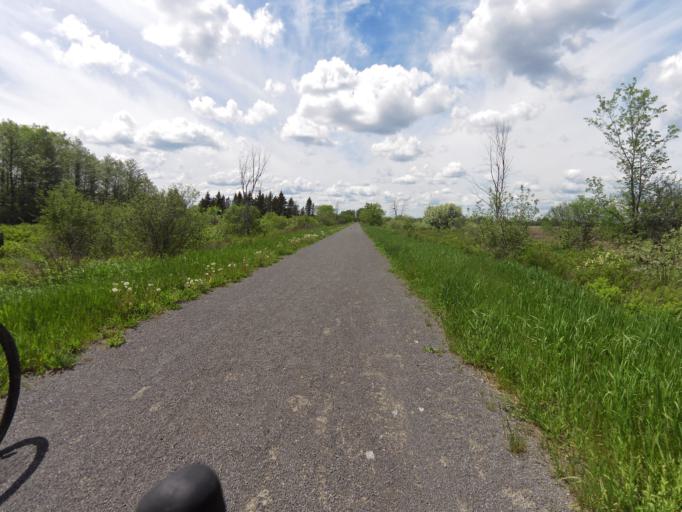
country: CA
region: Ontario
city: Ottawa
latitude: 45.4150
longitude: -75.5793
